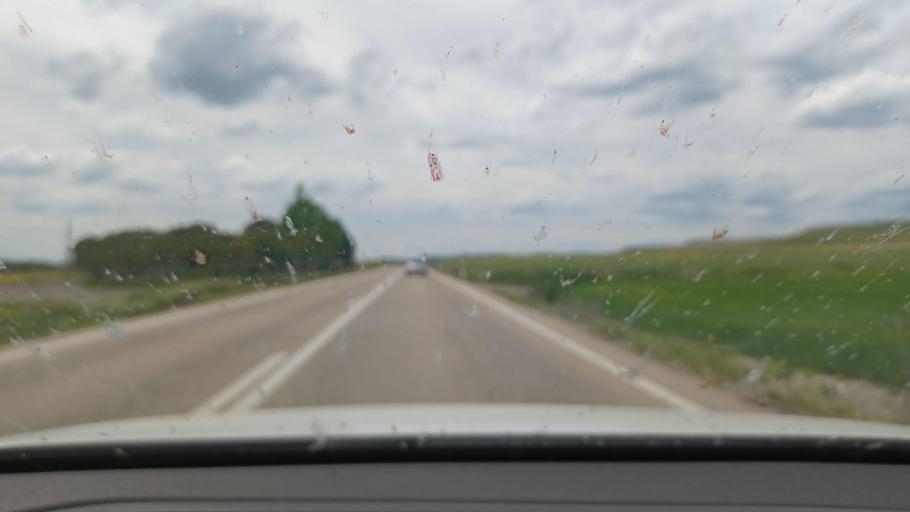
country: ES
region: Castille and Leon
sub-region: Provincia de Segovia
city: Cuellar
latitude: 41.3850
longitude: -4.2576
